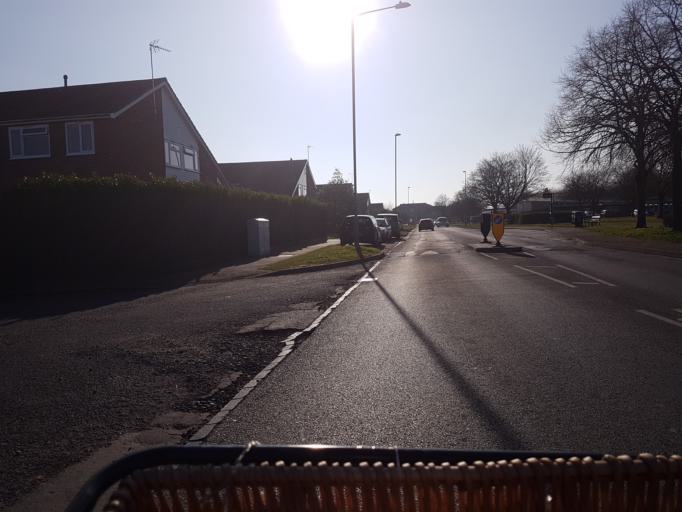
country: GB
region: England
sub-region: Cambridgeshire
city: Cambridge
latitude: 52.2274
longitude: 0.1302
